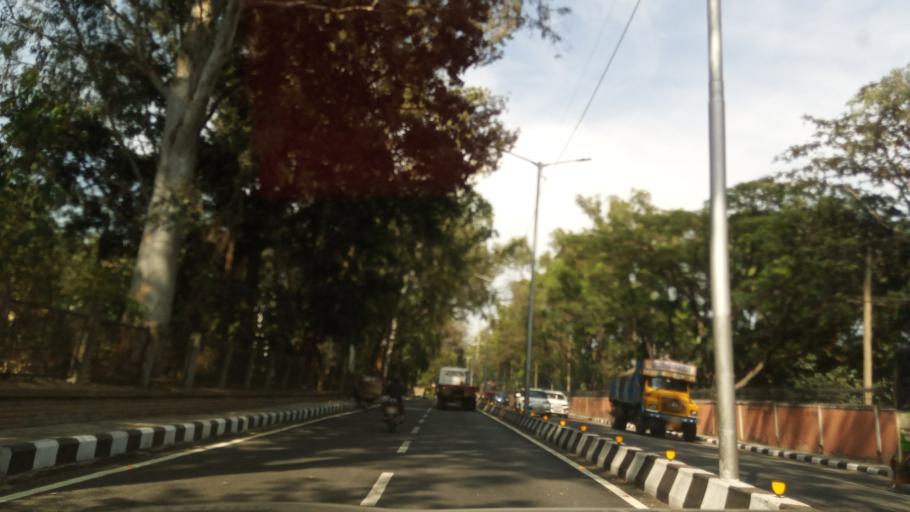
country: IN
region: Karnataka
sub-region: Bangalore Urban
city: Bangalore
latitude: 13.0342
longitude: 77.5411
